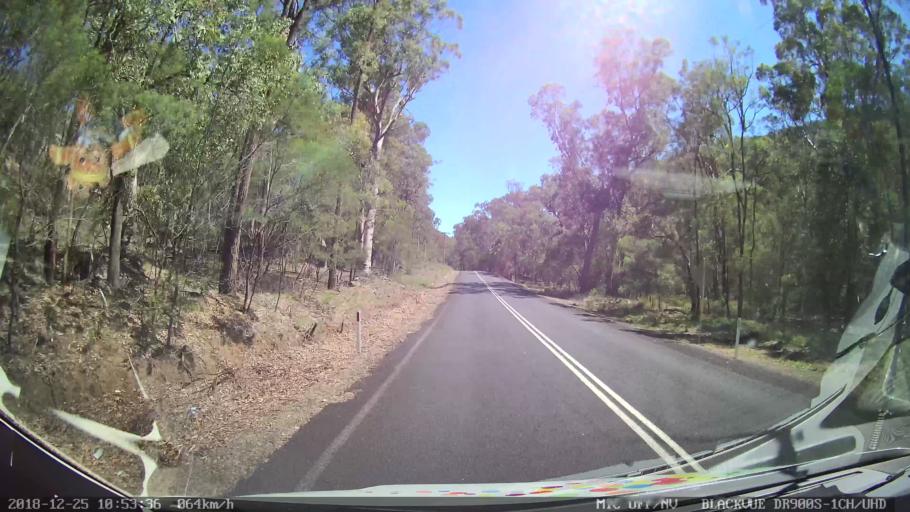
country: AU
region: New South Wales
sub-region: Upper Hunter Shire
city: Merriwa
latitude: -32.4185
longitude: 150.2732
